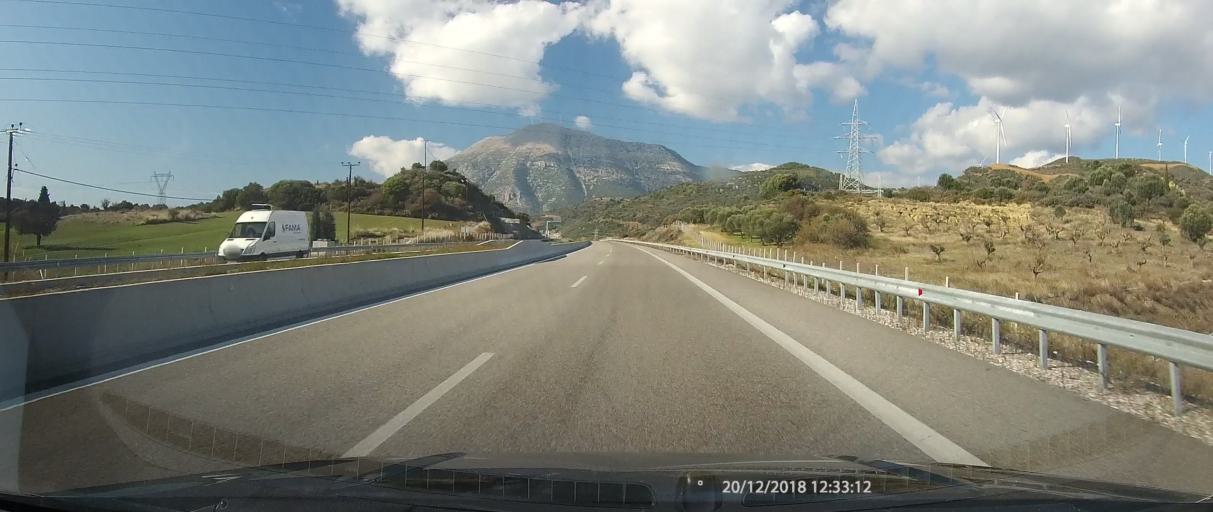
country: GR
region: West Greece
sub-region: Nomos Aitolias kai Akarnanias
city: Antirrio
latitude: 38.3485
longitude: 21.7481
